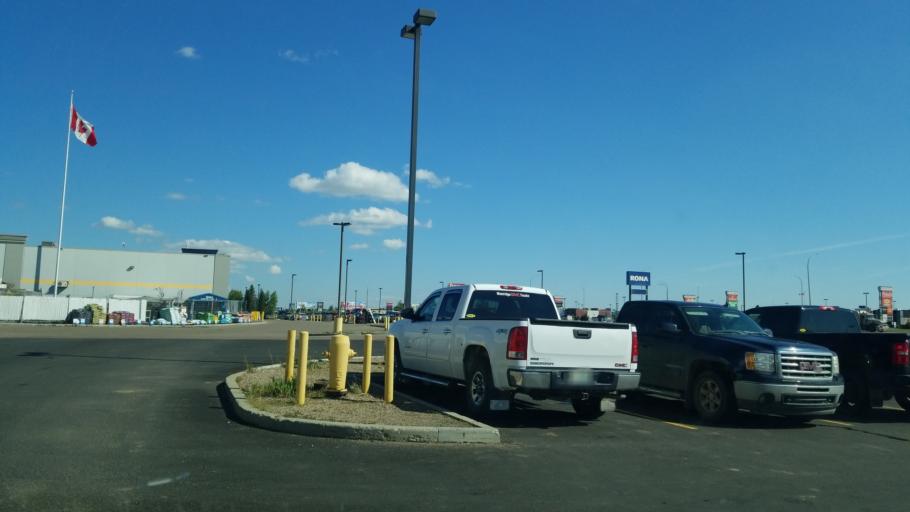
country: CA
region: Saskatchewan
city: Lloydminster
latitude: 53.2791
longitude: -110.0624
